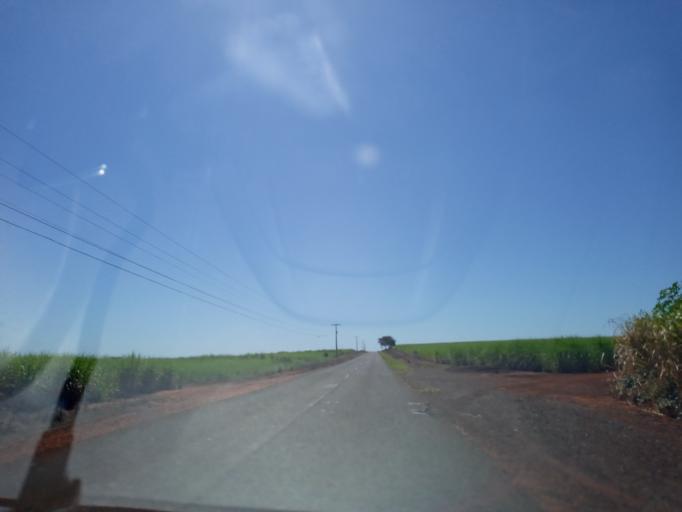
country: BR
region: Goias
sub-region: Itumbiara
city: Itumbiara
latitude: -18.4253
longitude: -49.1718
